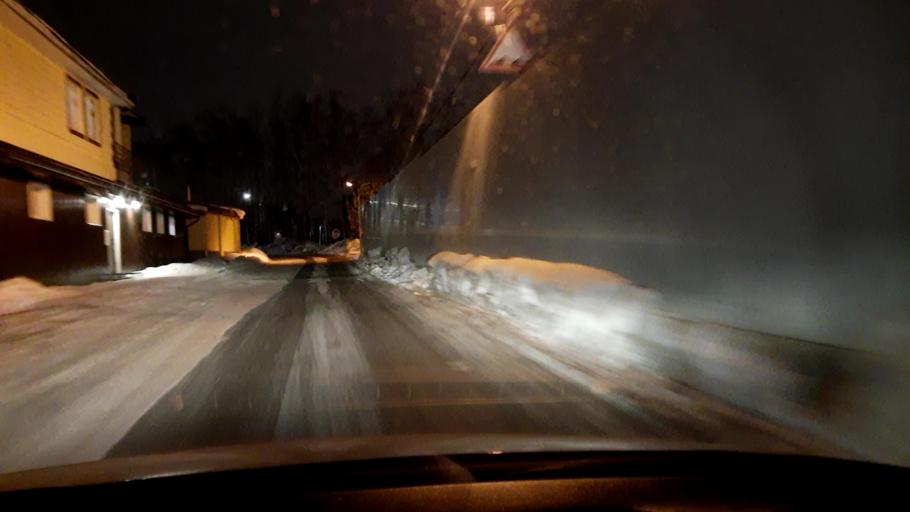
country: RU
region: Moskovskaya
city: Kommunarka
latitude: 55.5519
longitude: 37.5175
